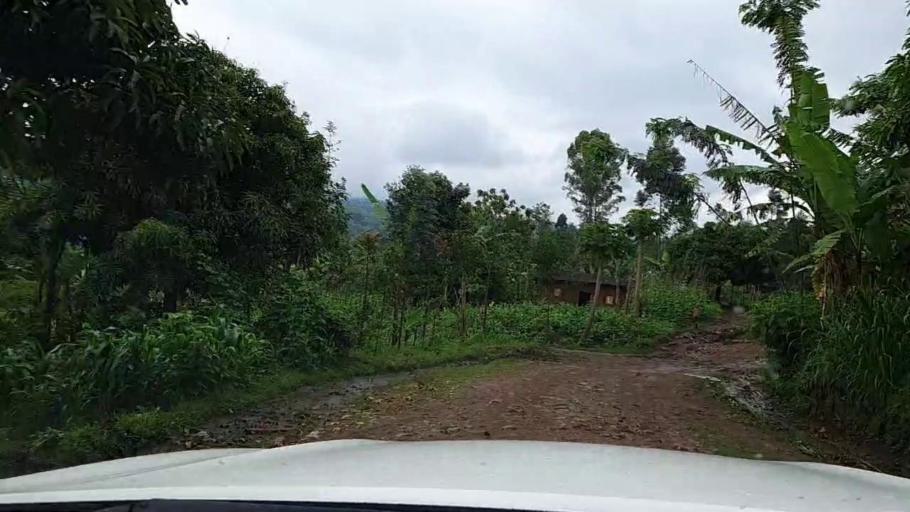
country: RW
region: Western Province
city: Cyangugu
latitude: -2.5499
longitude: 29.0383
